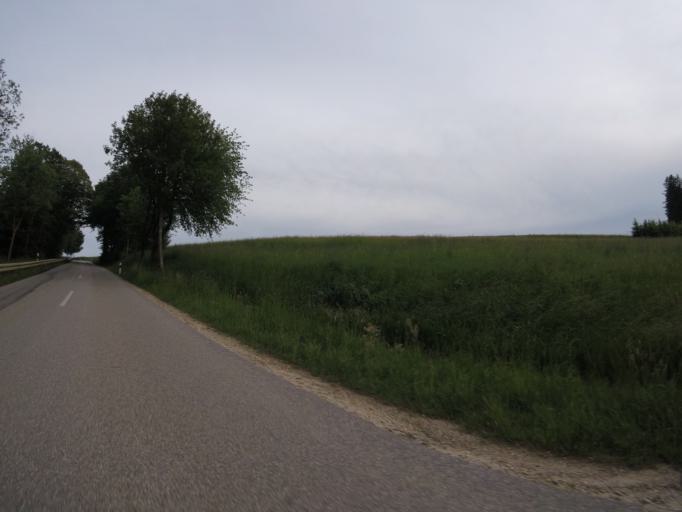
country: DE
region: Bavaria
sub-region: Upper Bavaria
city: Paunzhausen
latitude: 48.4939
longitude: 11.5406
